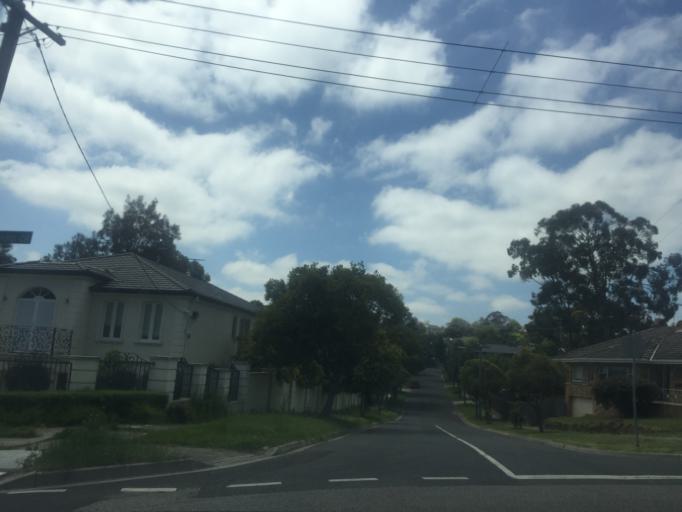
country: AU
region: Victoria
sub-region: Boroondara
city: Balwyn North
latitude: -37.8032
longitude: 145.0923
